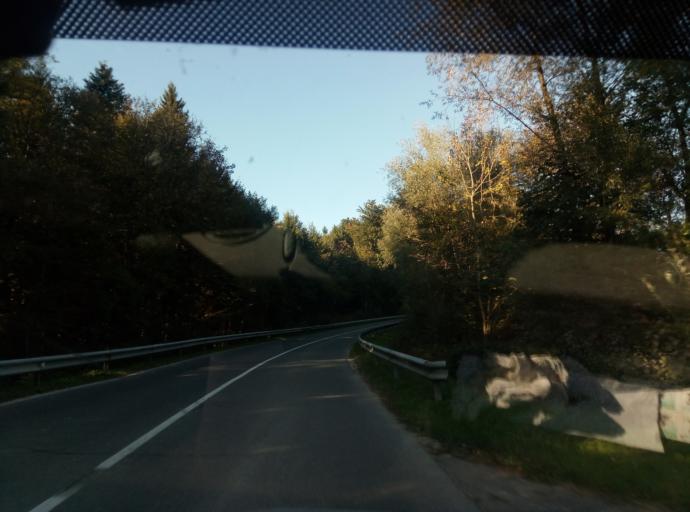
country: SI
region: Medvode
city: Zgornje Pirnice
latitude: 46.1357
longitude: 14.4762
